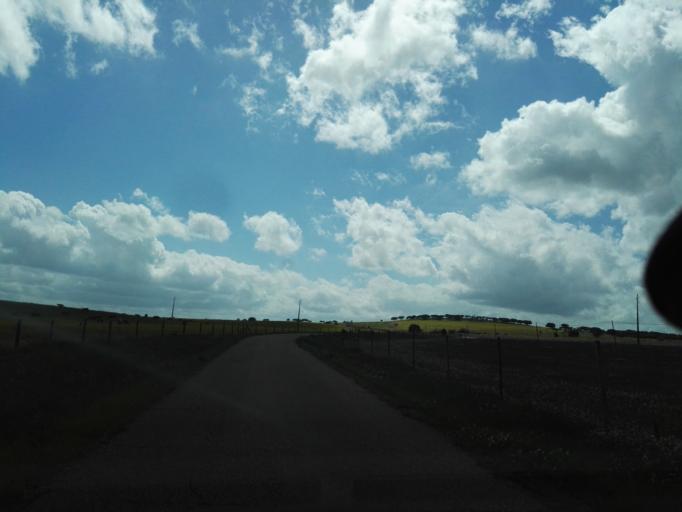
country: PT
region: Portalegre
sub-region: Elvas
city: Elvas
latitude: 38.9628
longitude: -7.1746
